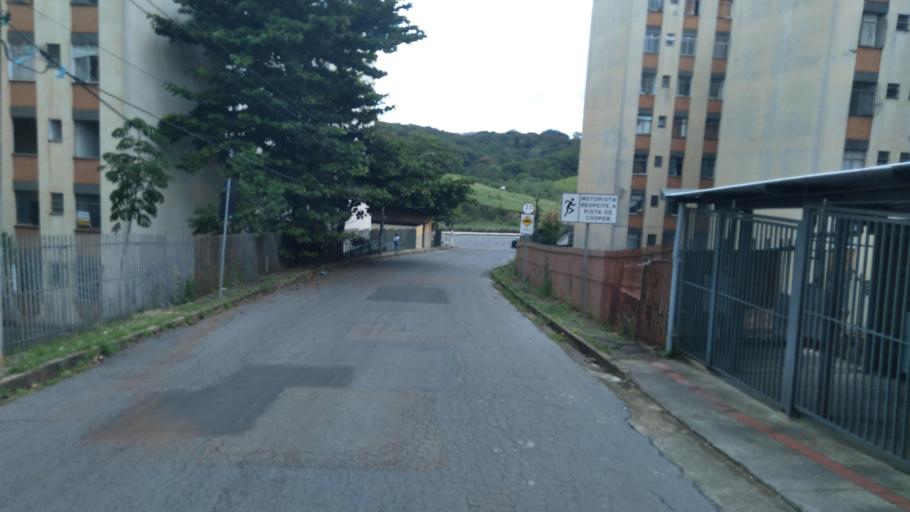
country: BR
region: Minas Gerais
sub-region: Contagem
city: Contagem
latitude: -19.9192
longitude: -44.0124
